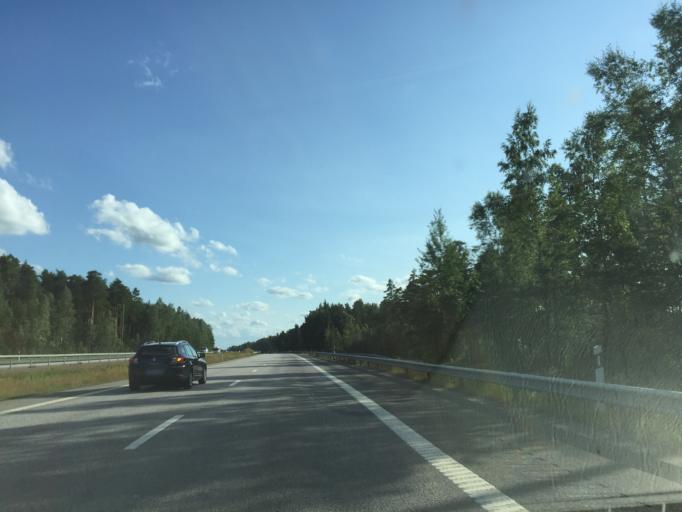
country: SE
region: OErebro
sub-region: Kumla Kommun
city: Kumla
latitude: 59.1378
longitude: 15.0818
